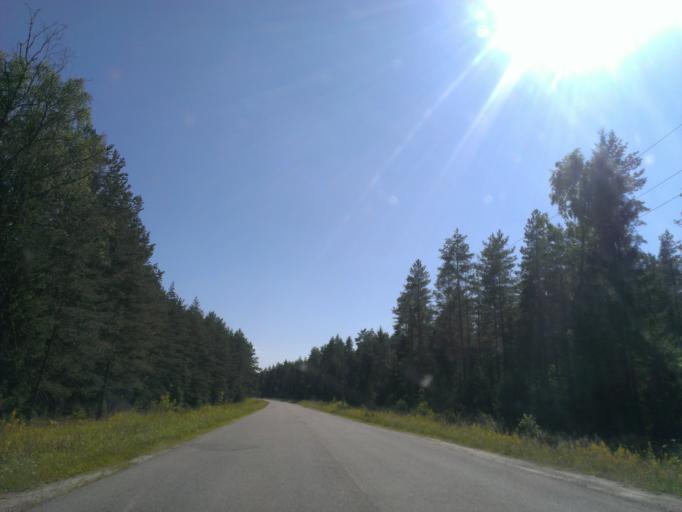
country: LV
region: Sigulda
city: Sigulda
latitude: 57.1157
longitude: 24.8258
